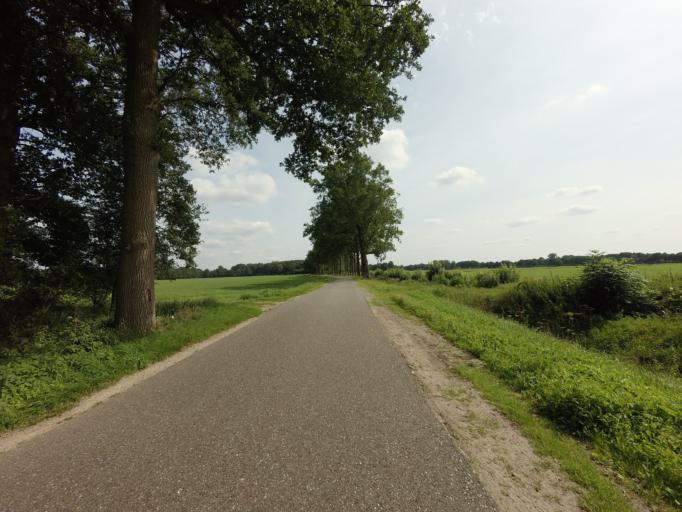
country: NL
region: Overijssel
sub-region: Gemeente Oldenzaal
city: Oldenzaal
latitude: 52.3973
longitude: 6.9170
